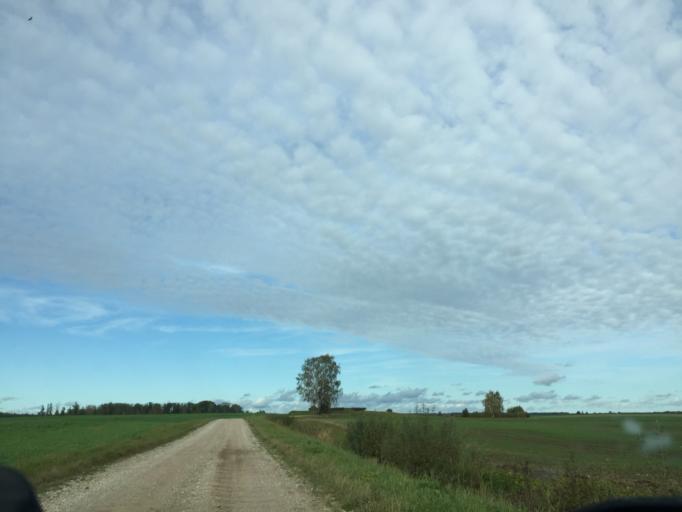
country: LV
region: Jaunpils
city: Jaunpils
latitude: 56.6507
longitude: 23.0775
